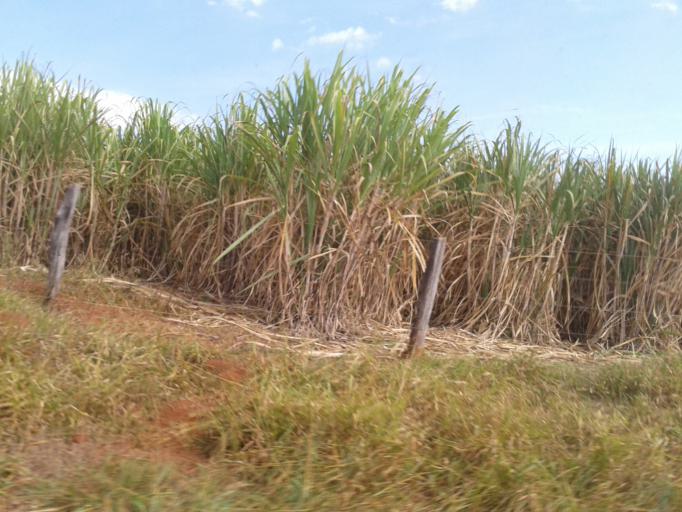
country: BR
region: Minas Gerais
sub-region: Ituiutaba
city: Ituiutaba
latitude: -19.0790
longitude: -49.3610
